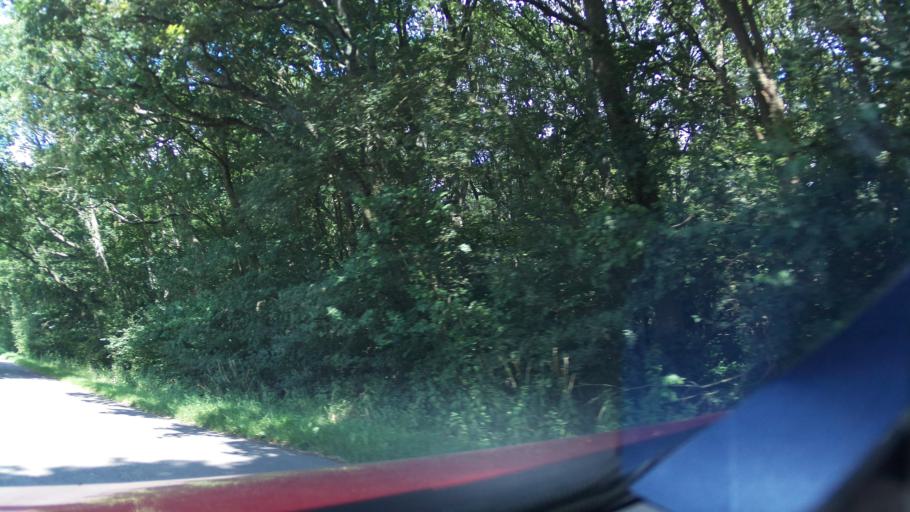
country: GB
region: England
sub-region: Wiltshire
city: Hankerton
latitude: 51.5926
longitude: -2.0314
